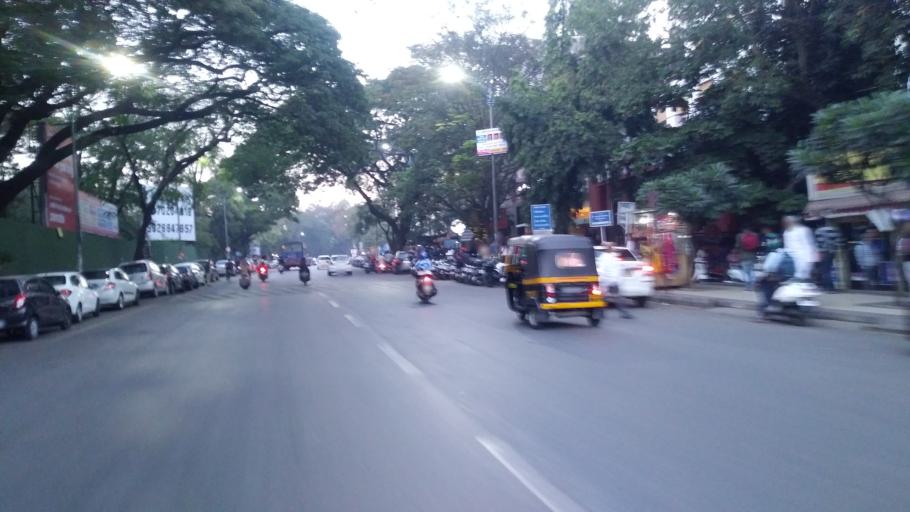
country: IN
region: Maharashtra
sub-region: Pune Division
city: Pune
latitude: 18.5208
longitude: 73.8411
